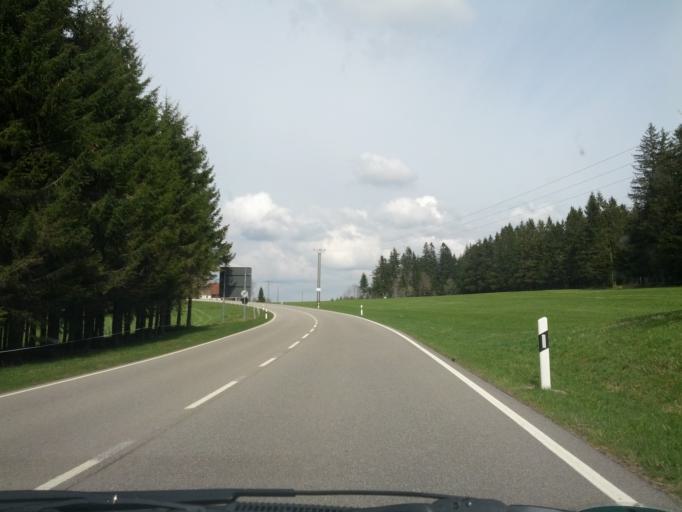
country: DE
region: Baden-Wuerttemberg
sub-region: Freiburg Region
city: Sankt Margen
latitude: 47.9731
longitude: 8.1275
